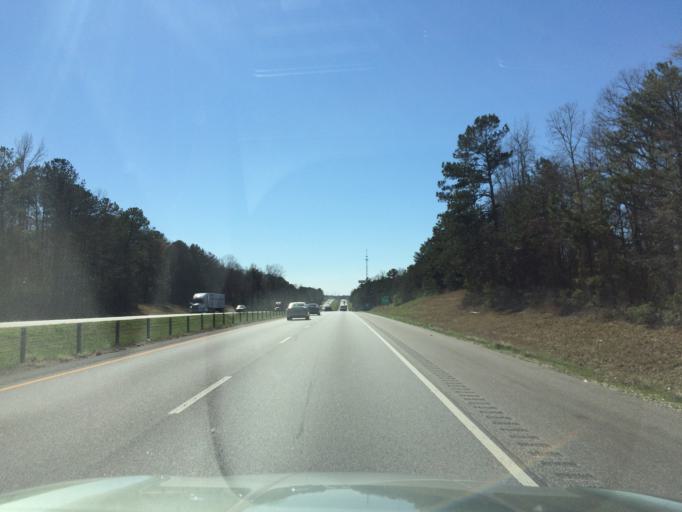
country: US
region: Alabama
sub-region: Lee County
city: Auburn
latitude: 32.5689
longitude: -85.4885
